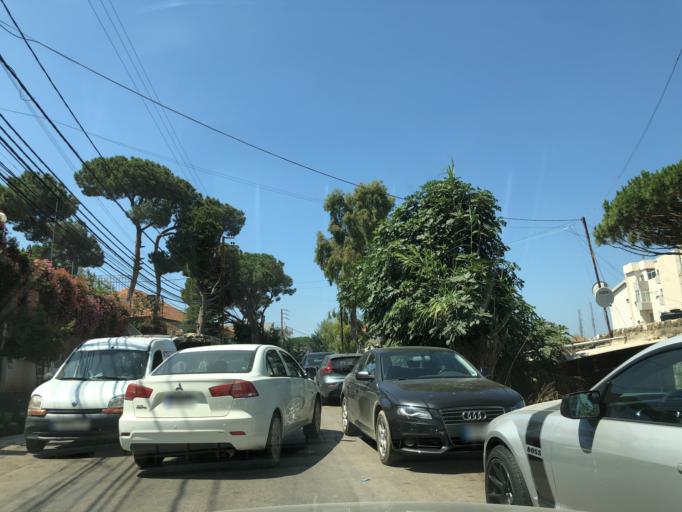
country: LB
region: Mont-Liban
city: Jdaidet el Matn
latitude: 33.8681
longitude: 35.6055
